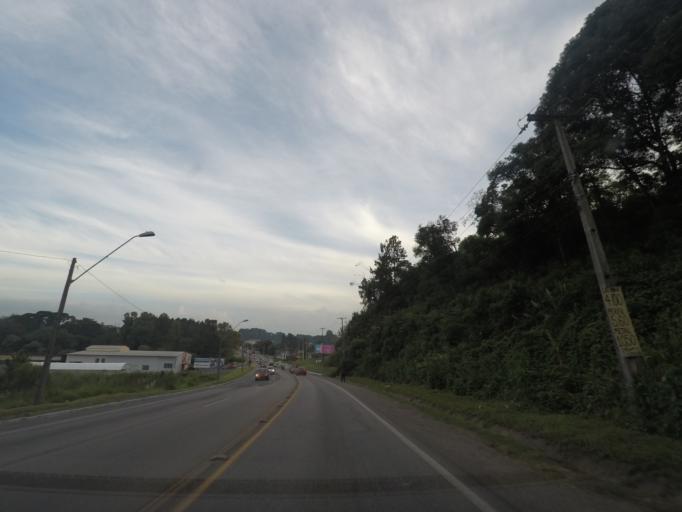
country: BR
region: Parana
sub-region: Colombo
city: Colombo
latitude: -25.3620
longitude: -49.2196
